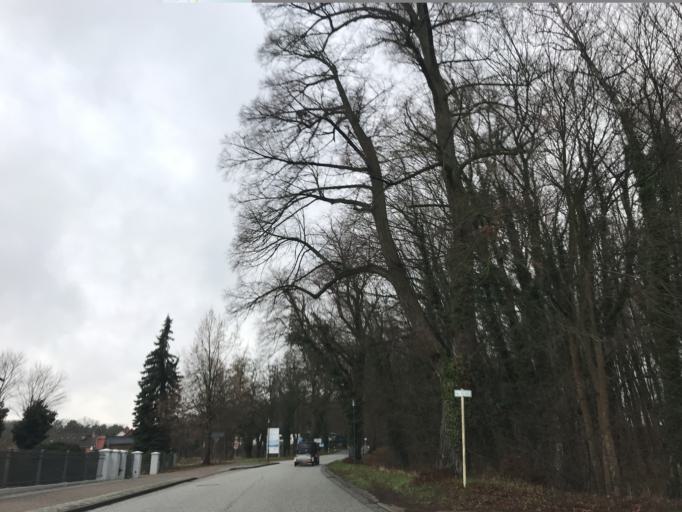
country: DE
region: Brandenburg
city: Lindow
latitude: 52.9766
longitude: 12.9854
